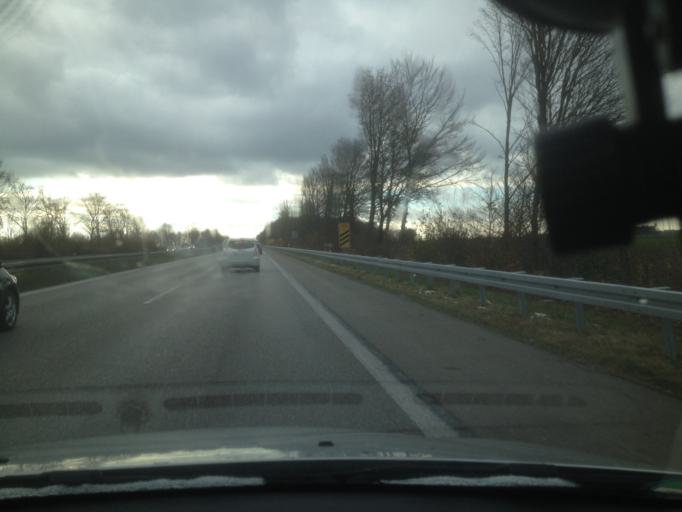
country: DE
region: Bavaria
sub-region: Swabia
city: Konigsbrunn
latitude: 48.2878
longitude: 10.8740
